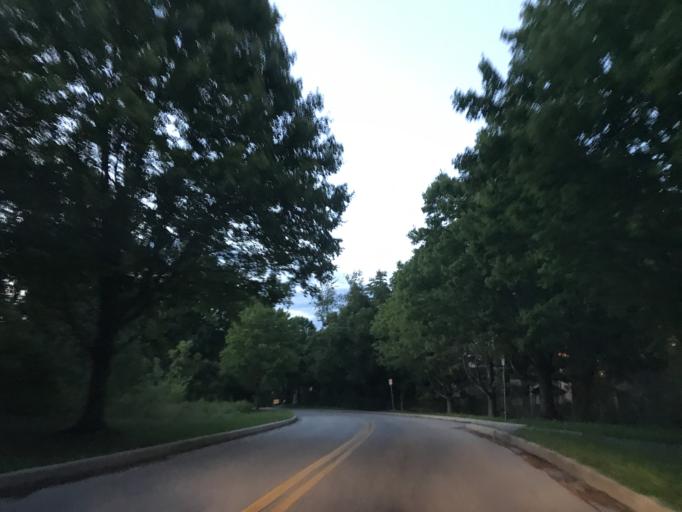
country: US
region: Maryland
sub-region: Anne Arundel County
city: Edgewater
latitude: 38.9773
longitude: -76.5536
